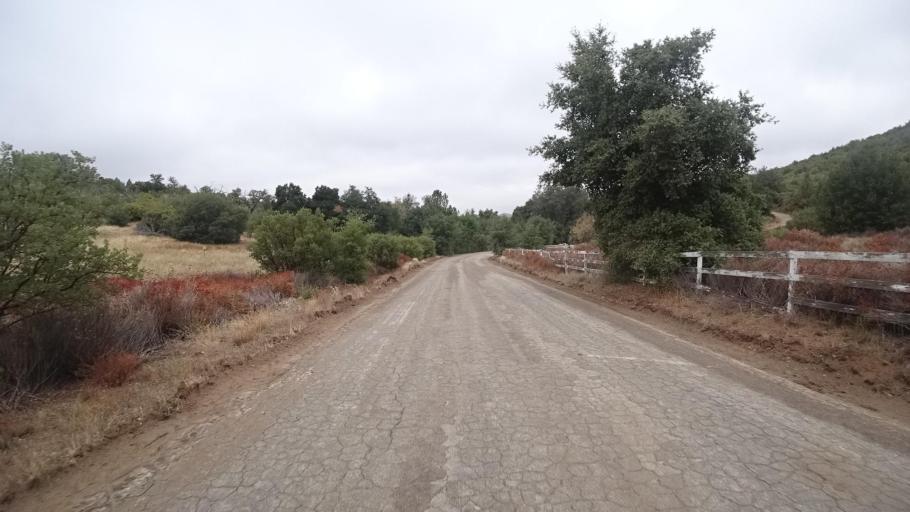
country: US
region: California
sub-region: San Diego County
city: Julian
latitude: 33.0175
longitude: -116.6353
